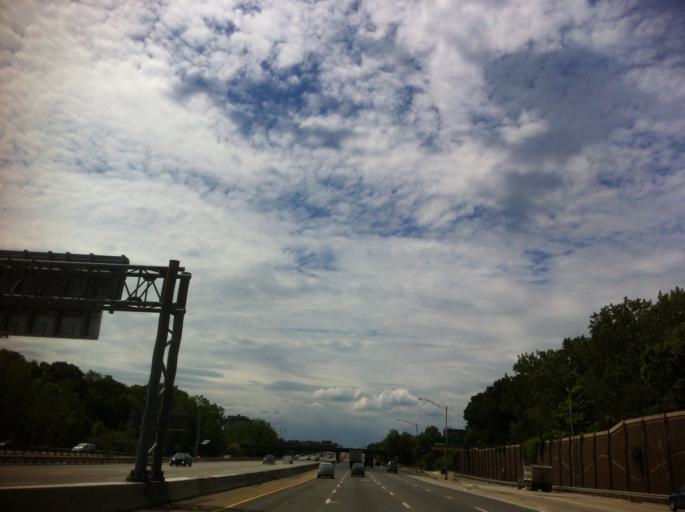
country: US
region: New Jersey
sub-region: Bergen County
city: Saddle Brook
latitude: 40.9027
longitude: -74.0895
